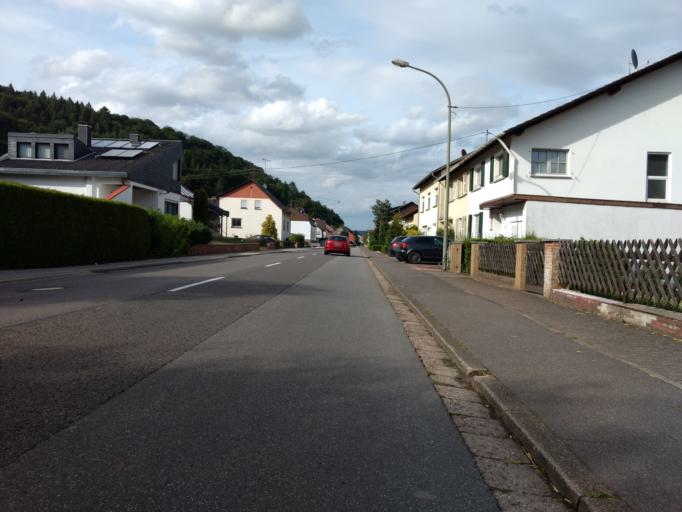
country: DE
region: Saarland
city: Beckingen
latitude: 49.4057
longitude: 6.7141
